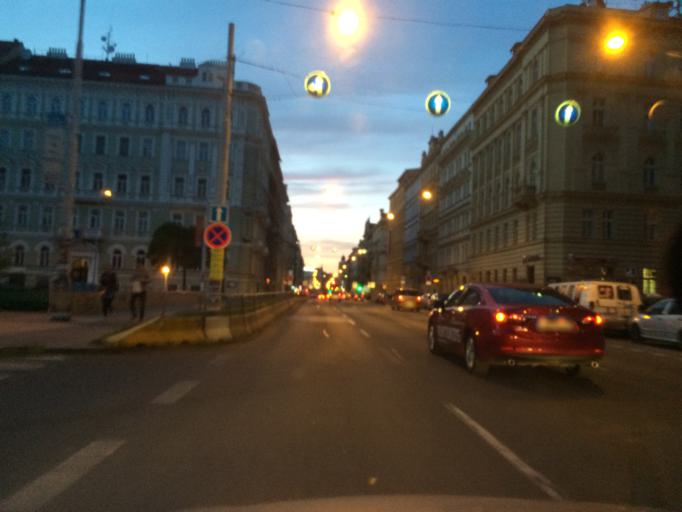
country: CZ
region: Praha
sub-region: Praha 2
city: Vysehrad
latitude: 50.0714
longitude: 14.4306
